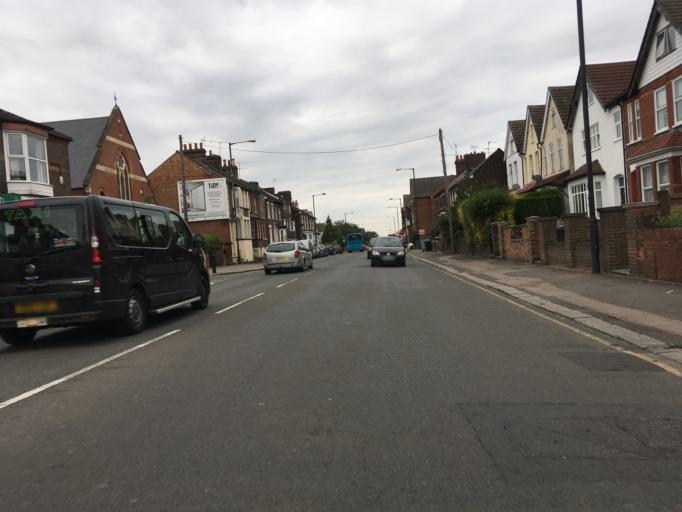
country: GB
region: England
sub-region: Central Bedfordshire
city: Dunstable
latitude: 51.8907
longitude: -0.5273
